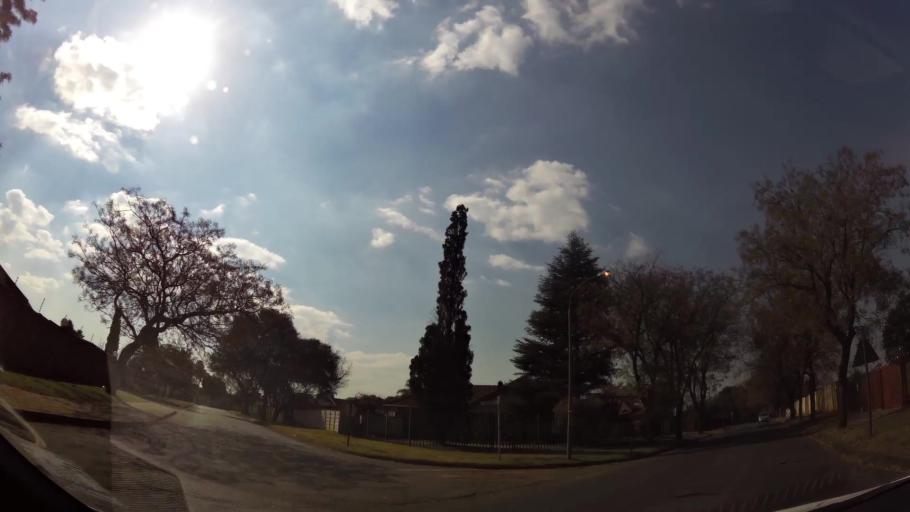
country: ZA
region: Gauteng
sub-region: Ekurhuleni Metropolitan Municipality
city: Boksburg
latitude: -26.1867
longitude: 28.2090
